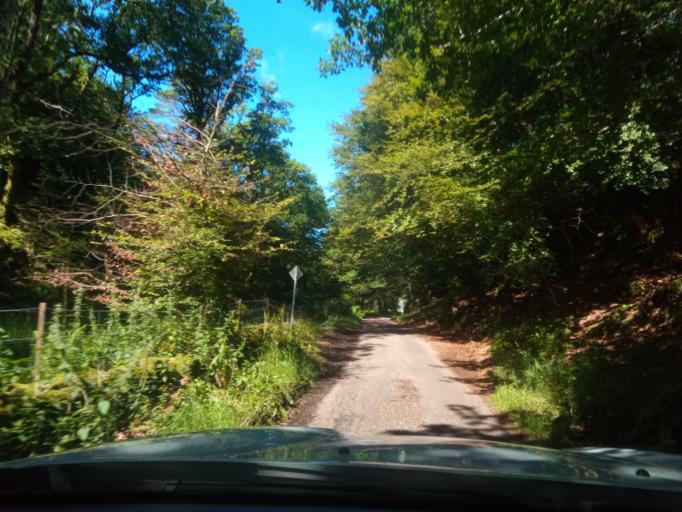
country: GB
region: Scotland
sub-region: Argyll and Bute
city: Isle Of Mull
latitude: 56.7579
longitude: -5.8092
